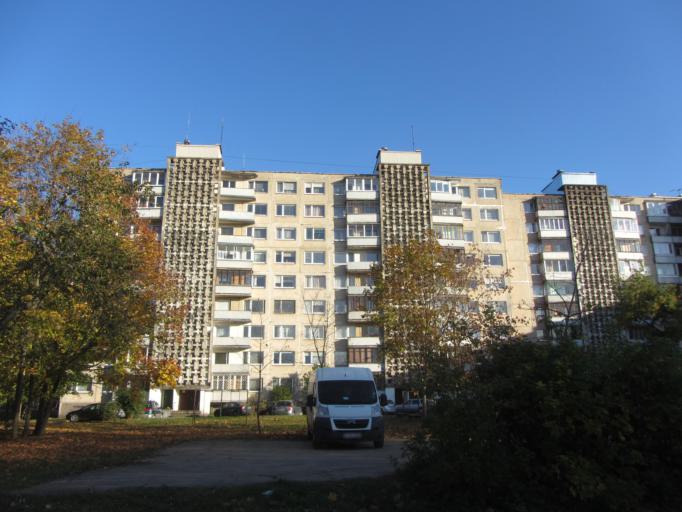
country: LT
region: Vilnius County
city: Lazdynai
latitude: 54.6871
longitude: 25.2025
